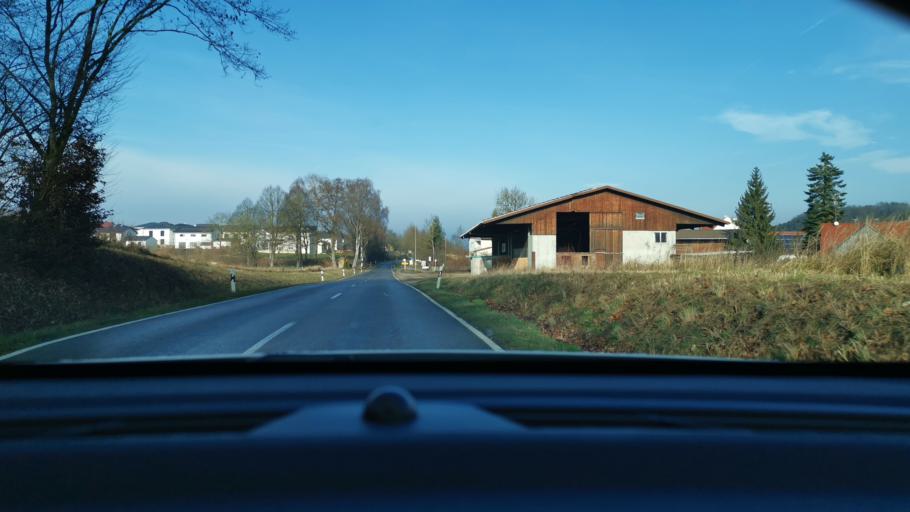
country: DE
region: Bavaria
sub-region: Swabia
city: Holzheim
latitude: 48.5833
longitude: 10.9633
